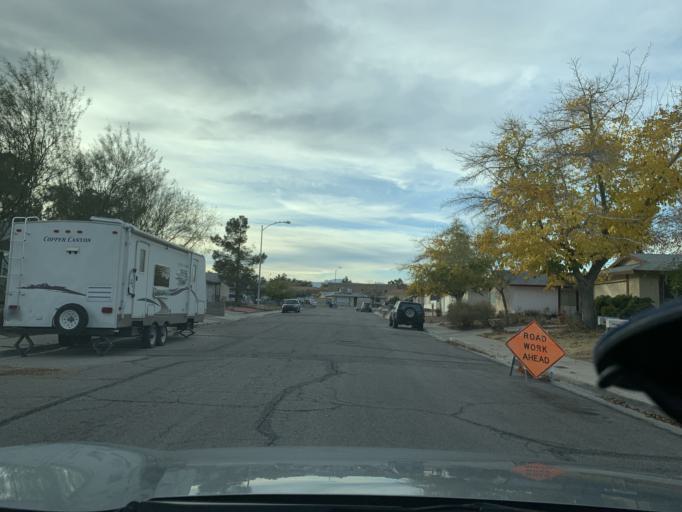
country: US
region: Nevada
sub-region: Clark County
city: Spring Valley
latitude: 36.0980
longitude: -115.2321
